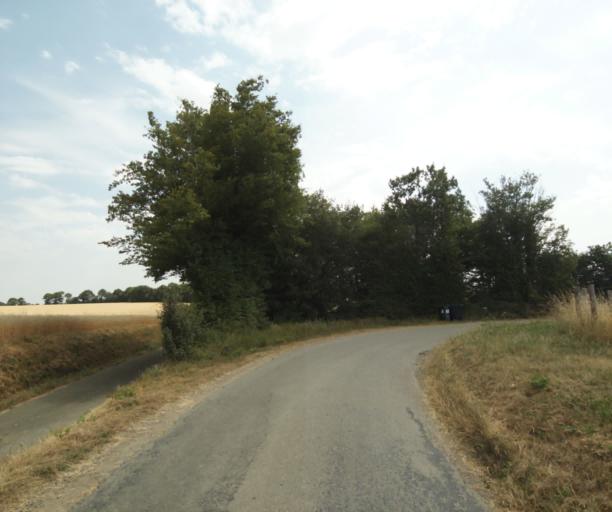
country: FR
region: Centre
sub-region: Departement d'Eure-et-Loir
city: La Bazoche-Gouet
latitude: 48.1881
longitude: 0.9794
